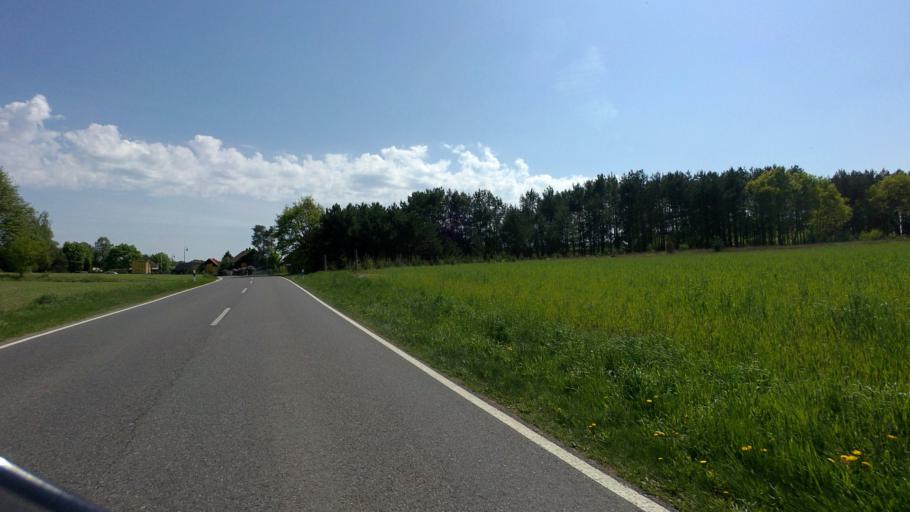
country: DE
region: Brandenburg
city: Lieberose
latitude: 51.9849
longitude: 14.2153
